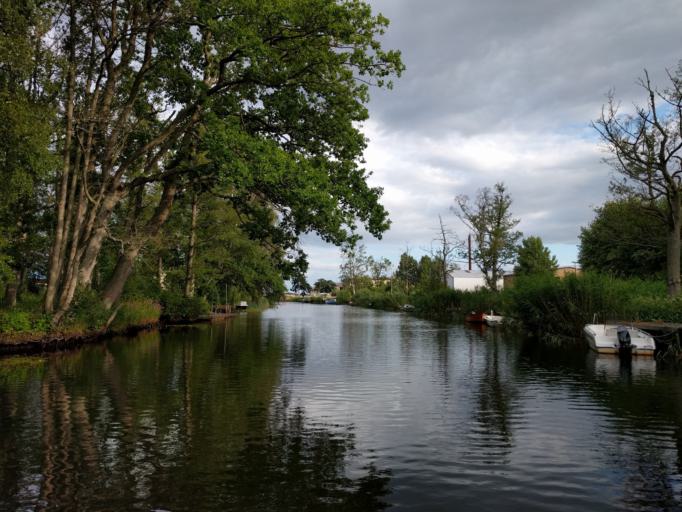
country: SE
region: Blekinge
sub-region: Ronneby Kommun
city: Ronneby
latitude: 56.1789
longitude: 15.2988
